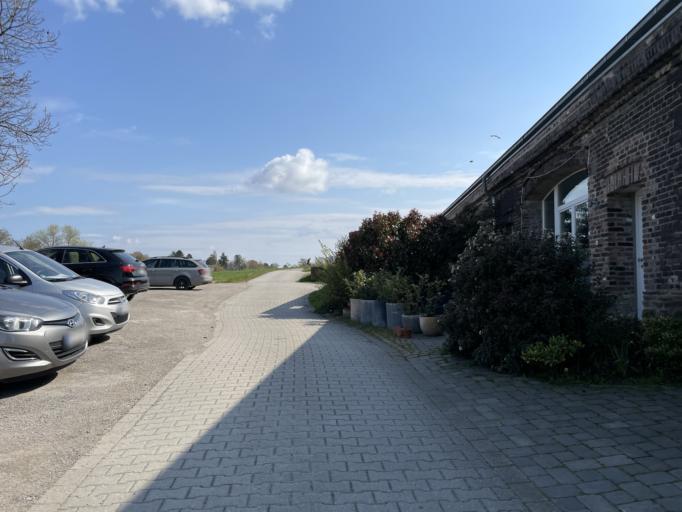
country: DE
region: North Rhine-Westphalia
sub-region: Regierungsbezirk Dusseldorf
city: Muelheim (Ruhr)
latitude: 51.4233
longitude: 6.9233
